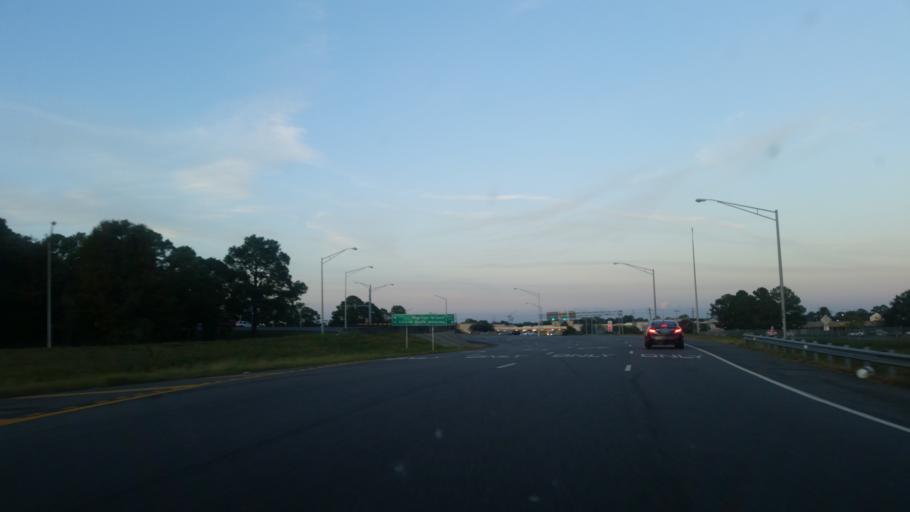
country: US
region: Alabama
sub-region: Mobile County
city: Prichard
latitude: 30.6746
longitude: -88.1267
